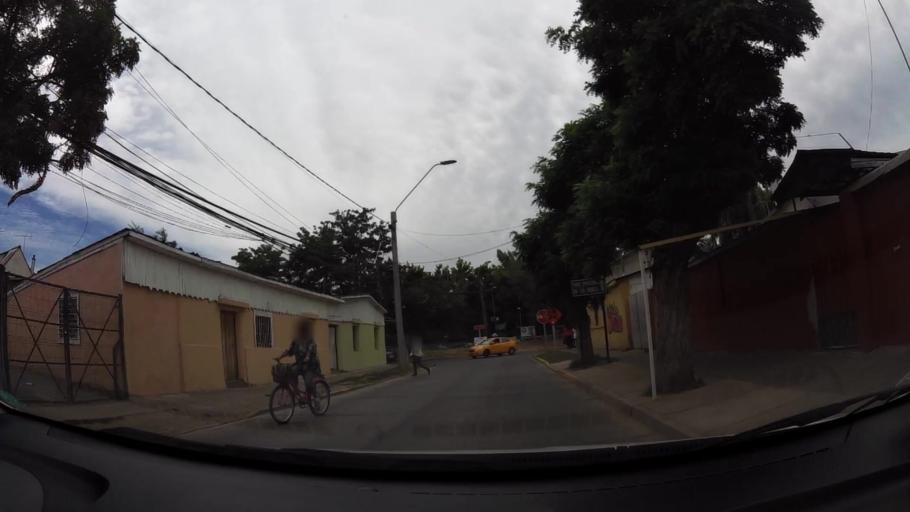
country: CL
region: O'Higgins
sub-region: Provincia de Cachapoal
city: Graneros
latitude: -34.0721
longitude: -70.7273
